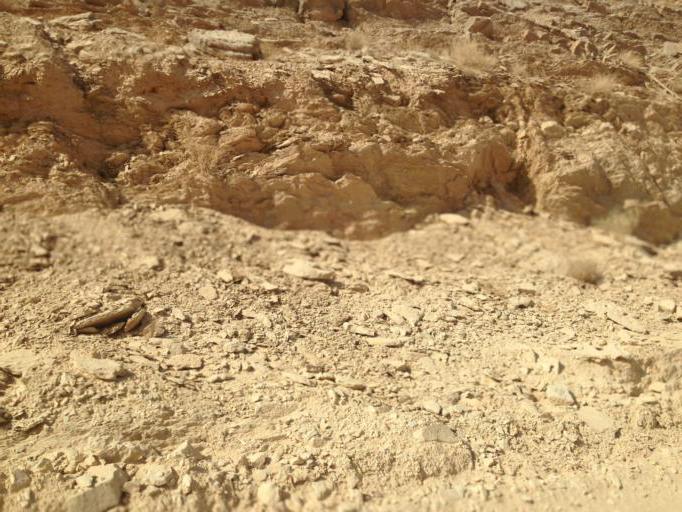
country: OM
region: Ash Sharqiyah
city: Al Qabil
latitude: 23.0699
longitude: 58.9587
